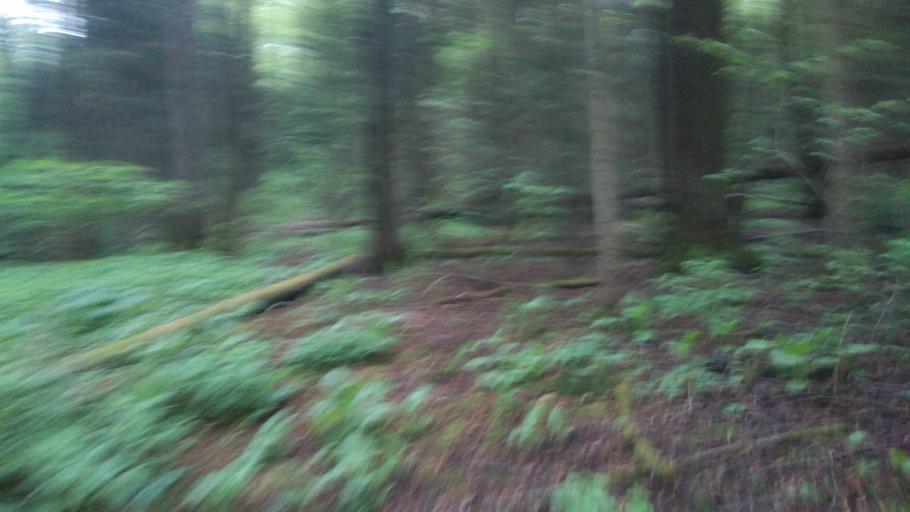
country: RU
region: Perm
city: Froly
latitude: 57.9605
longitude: 56.3087
